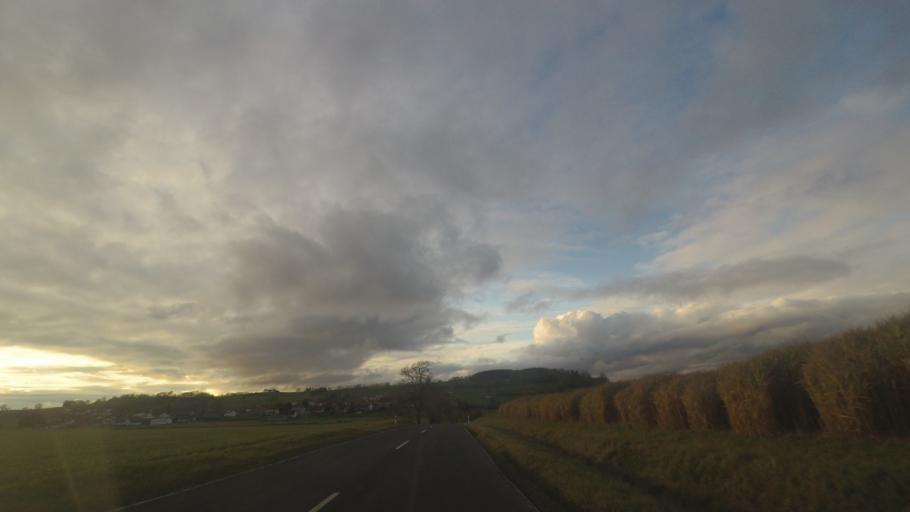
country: DE
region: Hesse
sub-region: Regierungsbezirk Giessen
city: Freiensteinau
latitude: 50.4596
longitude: 9.4140
